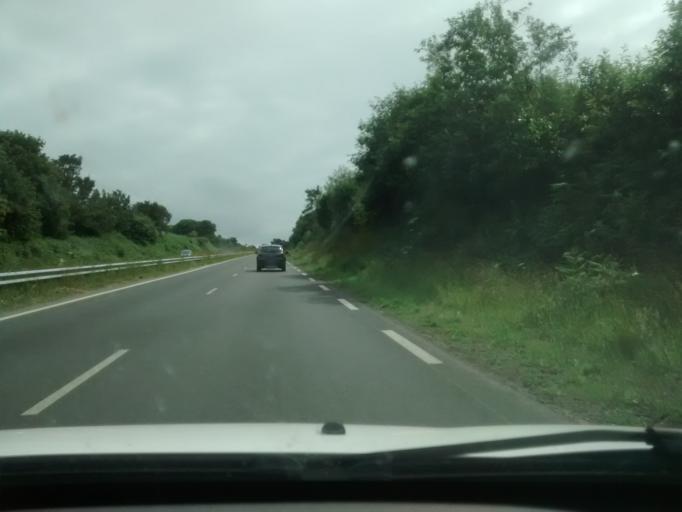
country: FR
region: Brittany
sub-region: Departement des Cotes-d'Armor
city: Saint-Quay-Perros
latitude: 48.7937
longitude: -3.4419
